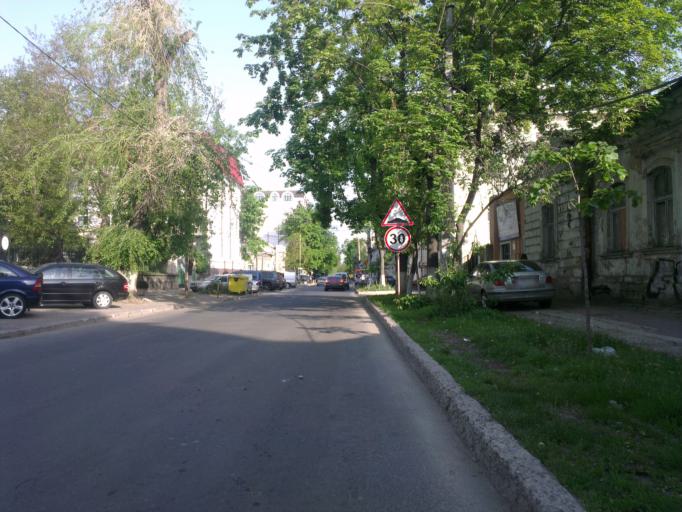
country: MD
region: Chisinau
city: Chisinau
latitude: 47.0293
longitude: 28.8297
